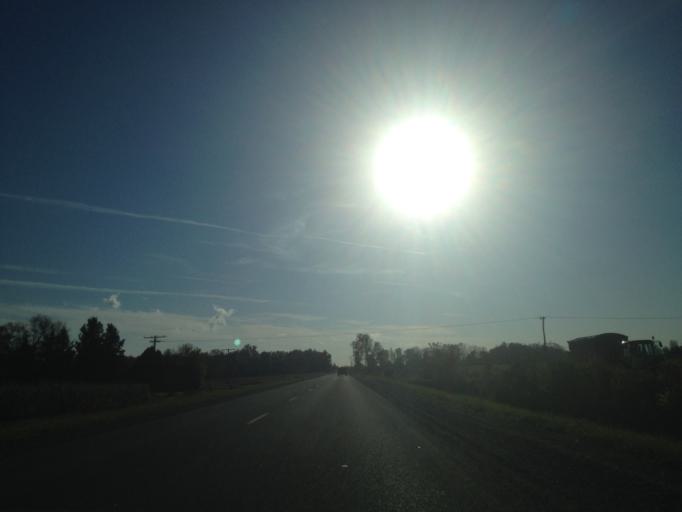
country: CA
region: Ontario
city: Delaware
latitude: 42.6426
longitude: -81.5528
